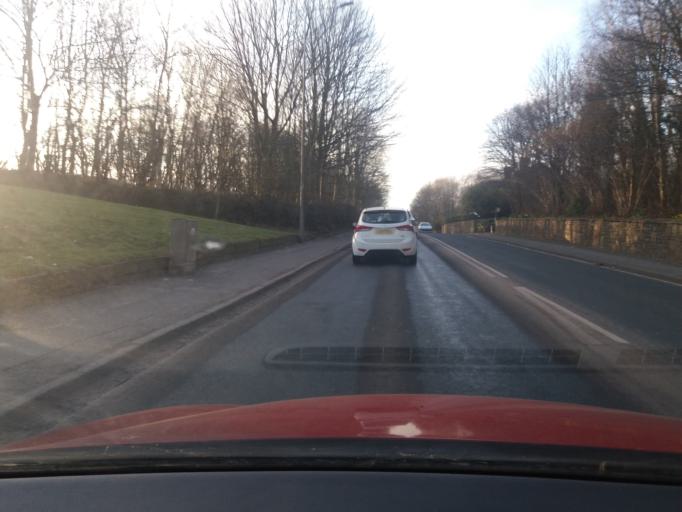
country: GB
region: England
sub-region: Lancashire
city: Euxton
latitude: 53.6565
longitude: -2.6545
